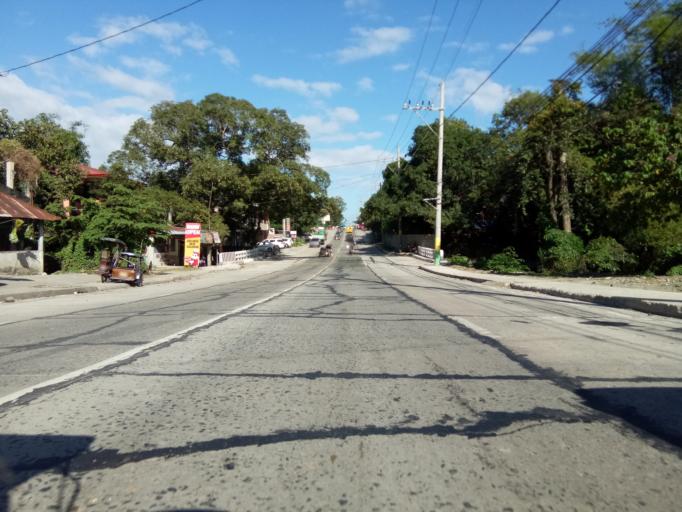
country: PH
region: Calabarzon
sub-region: Province of Cavite
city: Dasmarinas
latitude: 14.3518
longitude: 120.9767
